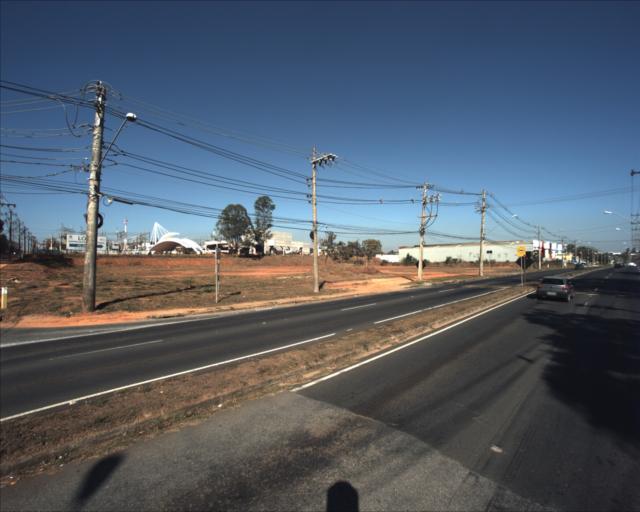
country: BR
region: Sao Paulo
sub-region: Sorocaba
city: Sorocaba
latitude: -23.4449
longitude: -47.4172
